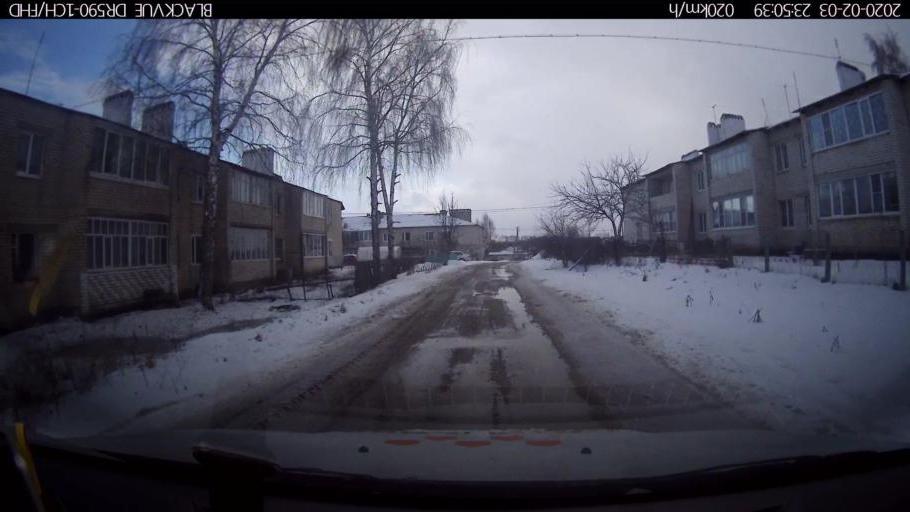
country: RU
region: Nizjnij Novgorod
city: Dal'neye Konstantinovo
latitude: 55.8059
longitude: 44.0788
